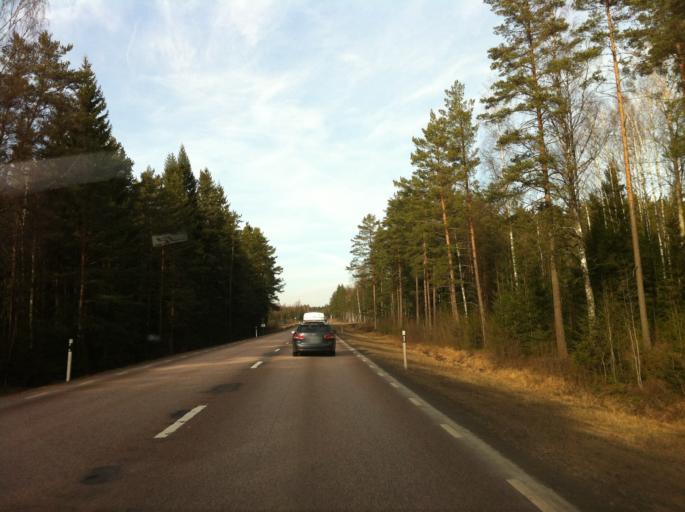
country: SE
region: Vaermland
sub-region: Kristinehamns Kommun
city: Bjorneborg
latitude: 59.1814
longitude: 14.1777
